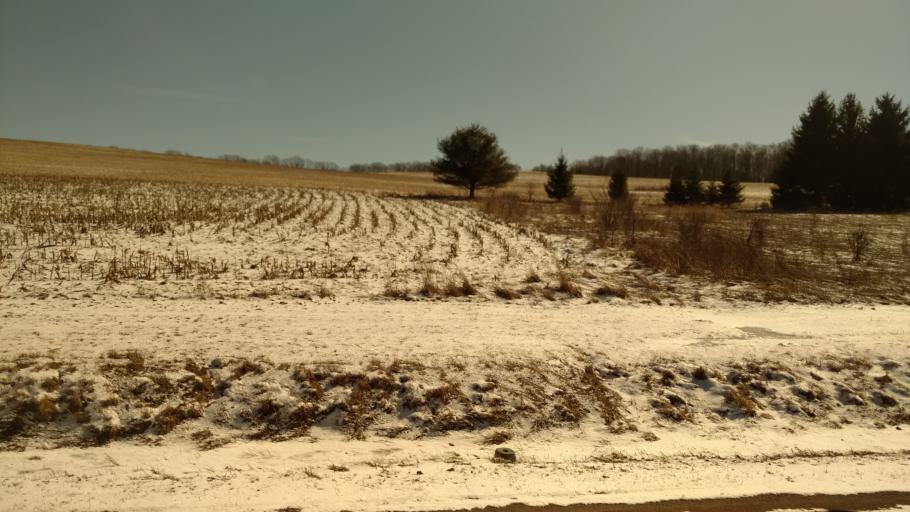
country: US
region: New York
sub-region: Allegany County
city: Wellsville
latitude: 42.0798
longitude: -78.0066
